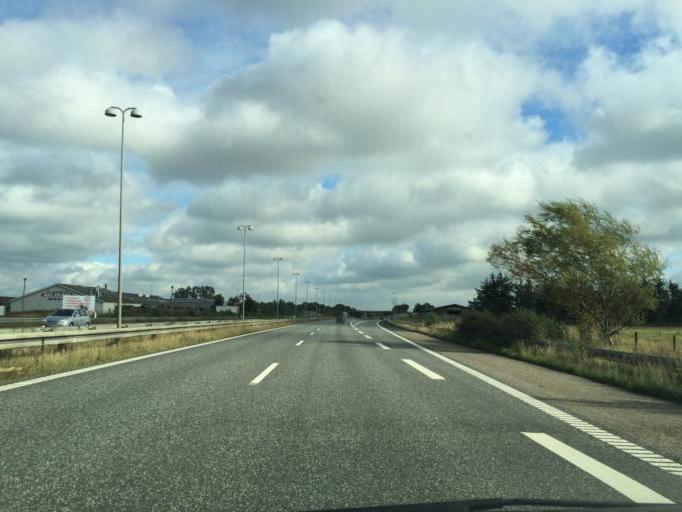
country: DK
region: North Denmark
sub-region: Alborg Kommune
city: Vestbjerg
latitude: 57.0838
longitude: 9.9681
